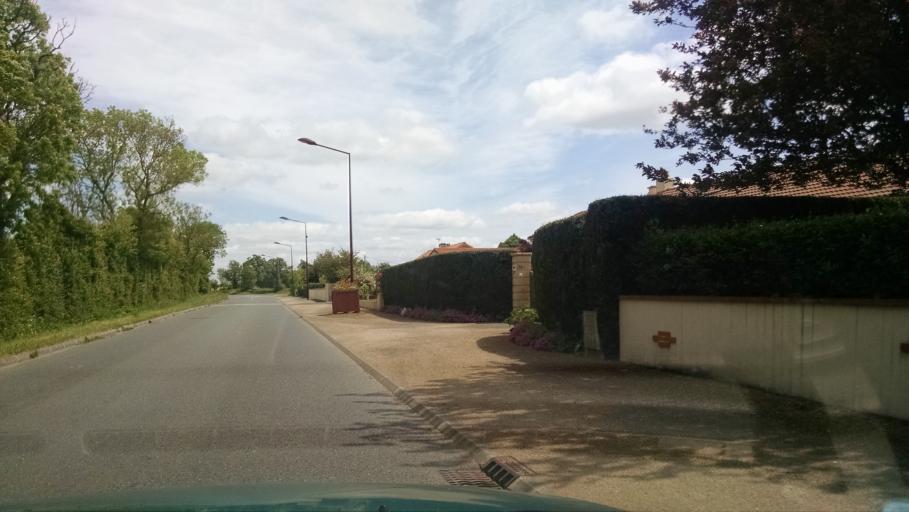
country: FR
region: Pays de la Loire
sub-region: Departement de la Loire-Atlantique
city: Saint-Hilaire-de-Clisson
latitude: 47.0607
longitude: -1.3037
